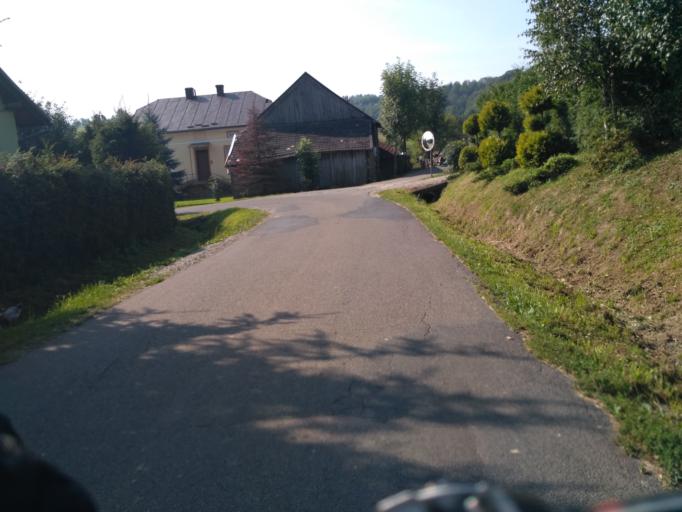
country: PL
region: Subcarpathian Voivodeship
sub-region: Powiat brzozowski
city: Golcowa
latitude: 49.7762
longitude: 22.0142
